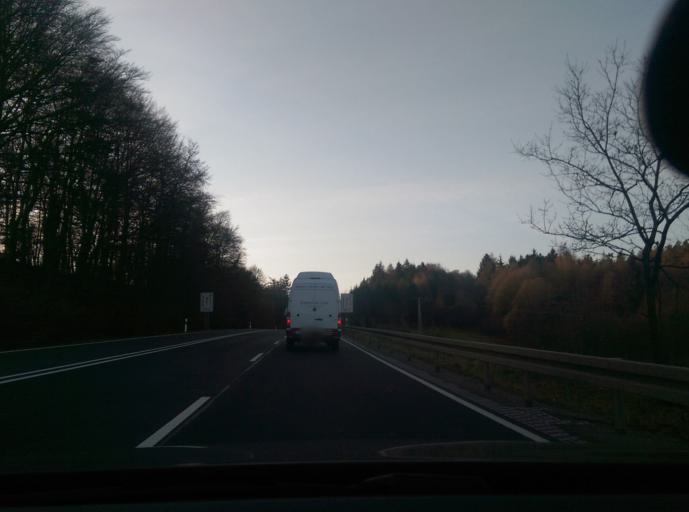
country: DE
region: Thuringia
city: Gerstungen
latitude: 51.0188
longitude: 10.0536
